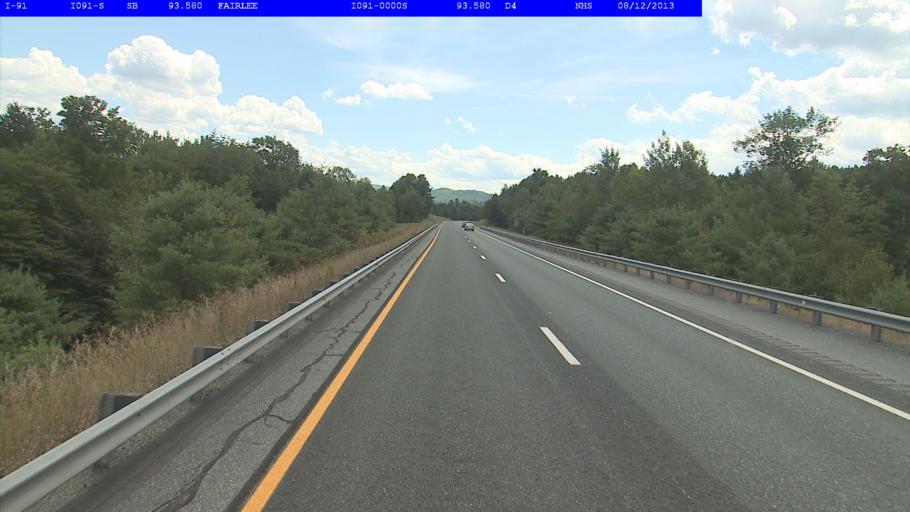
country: US
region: New Hampshire
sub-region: Grafton County
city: Orford
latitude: 43.9272
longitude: -72.1346
